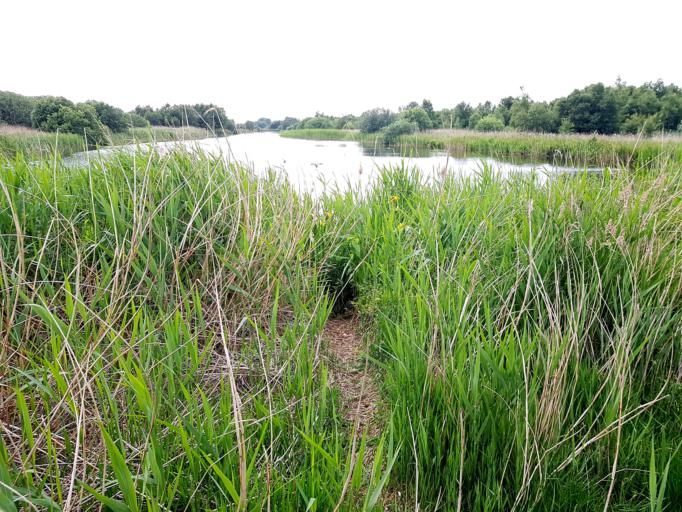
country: NL
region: Friesland
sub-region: Gemeente Smallingerland
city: Oudega
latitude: 53.0874
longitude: 5.9609
